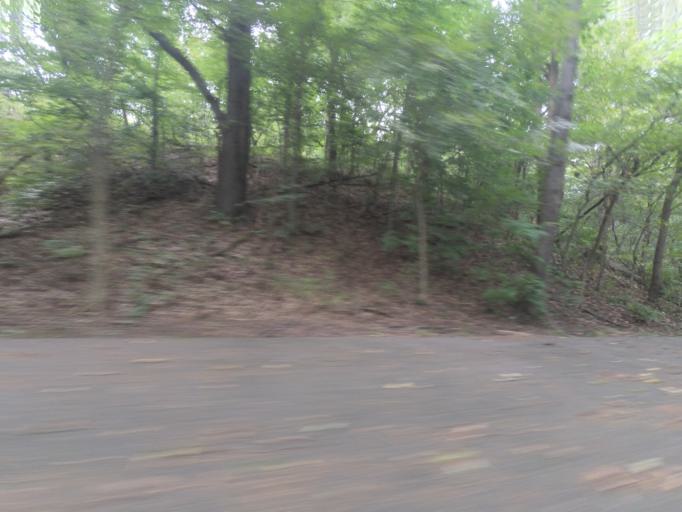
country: US
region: West Virginia
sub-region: Cabell County
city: Huntington
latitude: 38.4166
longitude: -82.3950
